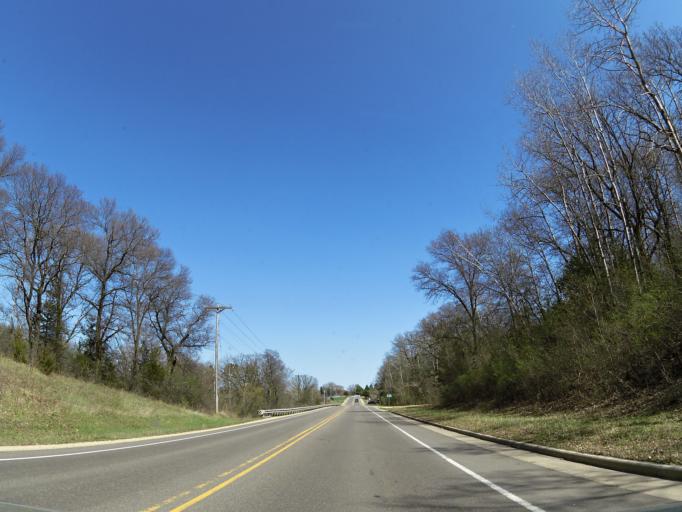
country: US
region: Wisconsin
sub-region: Saint Croix County
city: Hudson
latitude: 44.9594
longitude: -92.6869
